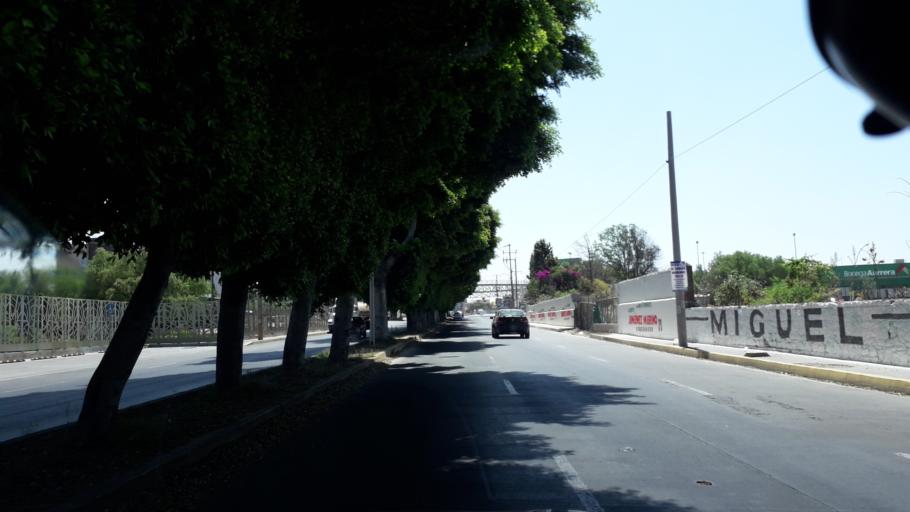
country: MX
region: Puebla
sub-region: Cuautlancingo
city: Sanctorum
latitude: 19.0914
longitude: -98.2316
